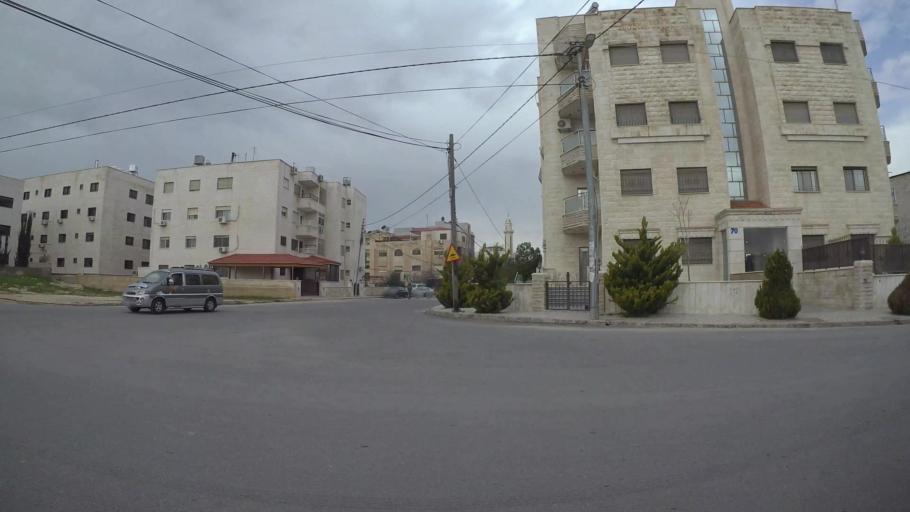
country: JO
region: Amman
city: Umm as Summaq
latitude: 31.8933
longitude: 35.8448
